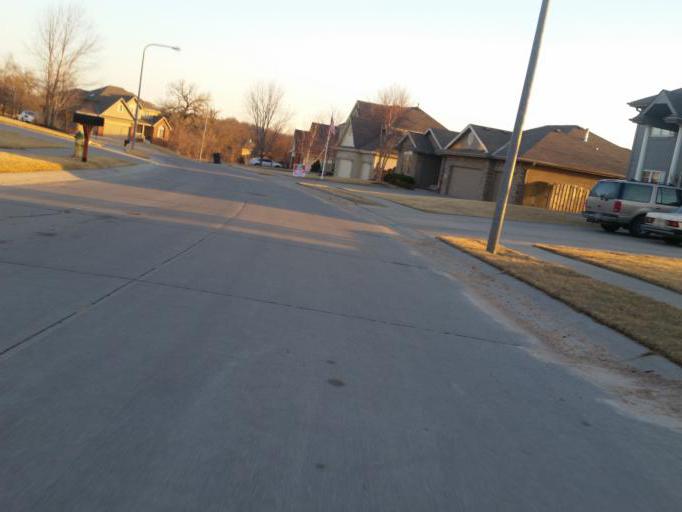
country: US
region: Nebraska
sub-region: Sarpy County
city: Papillion
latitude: 41.1547
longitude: -95.9988
